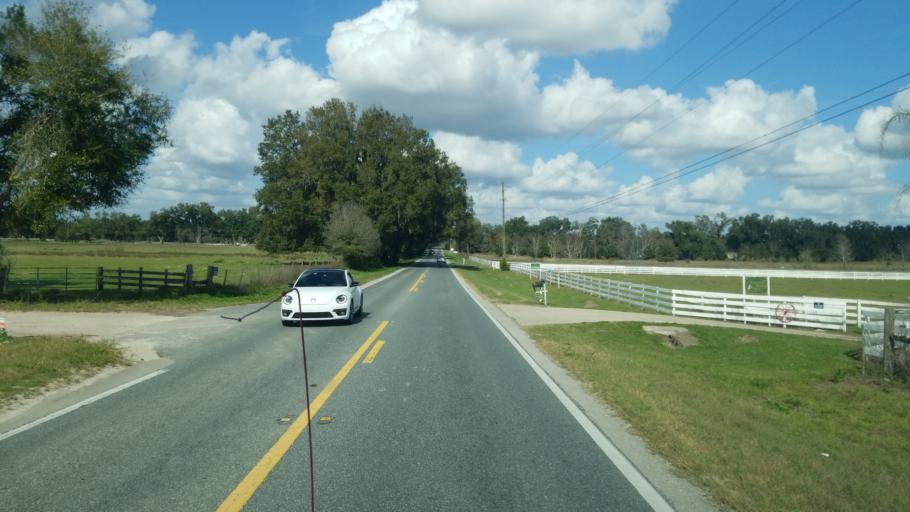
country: US
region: Florida
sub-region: Marion County
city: Belleview
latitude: 28.9854
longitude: -82.1199
